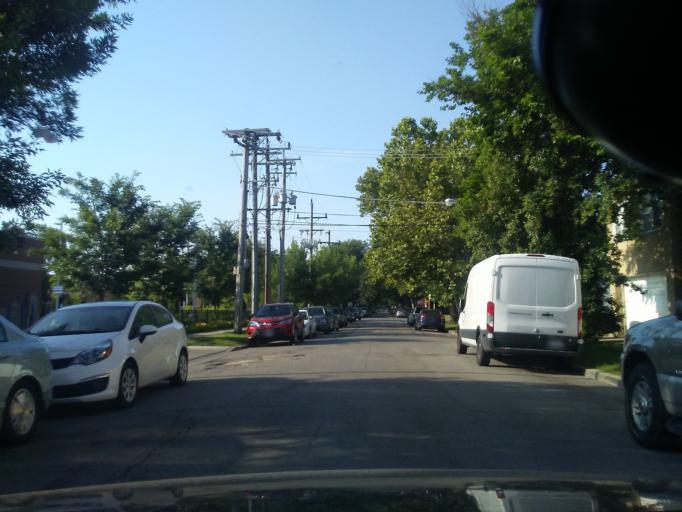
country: US
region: Illinois
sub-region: Cook County
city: Oak Park
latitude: 41.9314
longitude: -87.7442
